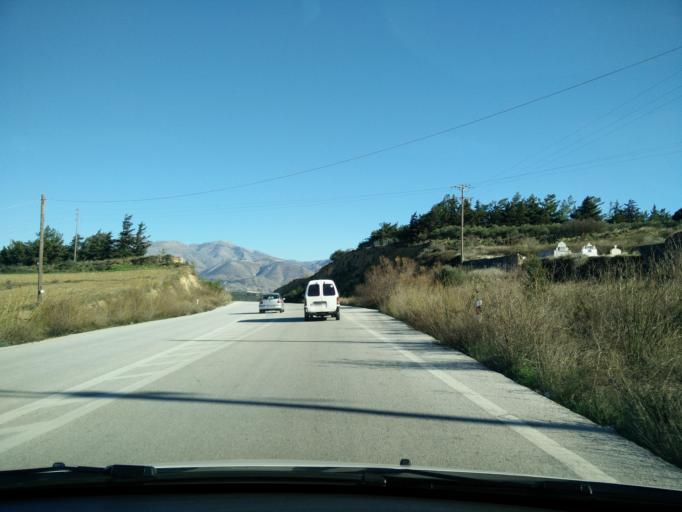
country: GR
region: Crete
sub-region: Nomos Irakleiou
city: Arkalochori
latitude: 35.1346
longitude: 25.2659
